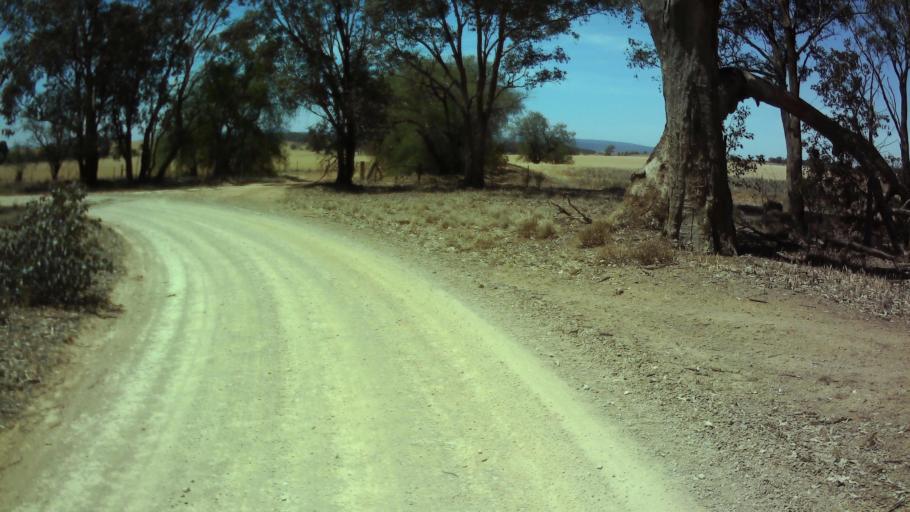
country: AU
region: New South Wales
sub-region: Weddin
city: Grenfell
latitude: -33.9284
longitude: 148.1786
